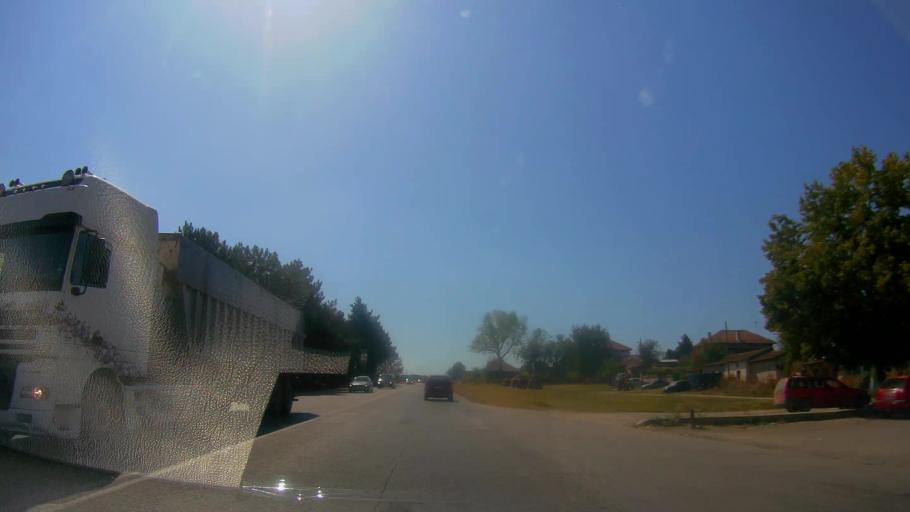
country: BG
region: Veliko Turnovo
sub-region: Obshtina Gorna Oryakhovitsa
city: Purvomaytsi
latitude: 43.2656
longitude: 25.6434
